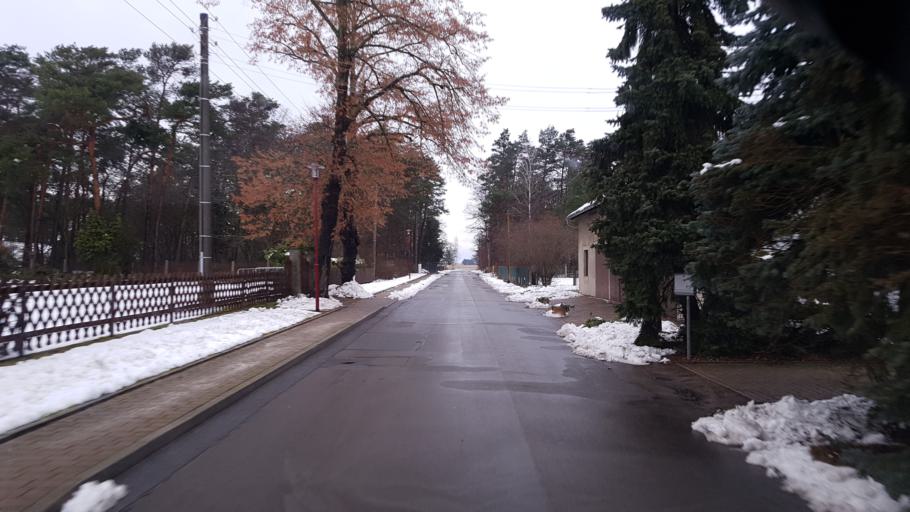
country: DE
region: Brandenburg
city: Luckau
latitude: 51.8626
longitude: 13.8132
